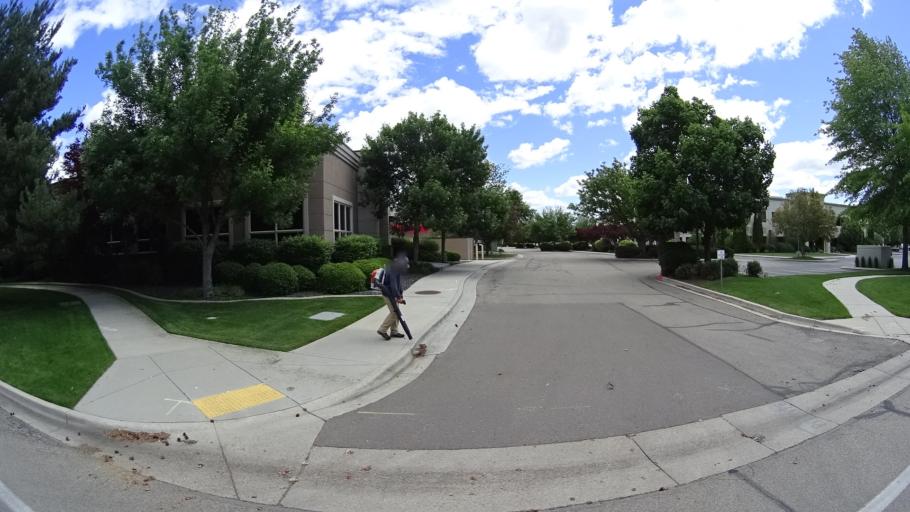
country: US
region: Idaho
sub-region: Ada County
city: Eagle
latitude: 43.6619
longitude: -116.3392
